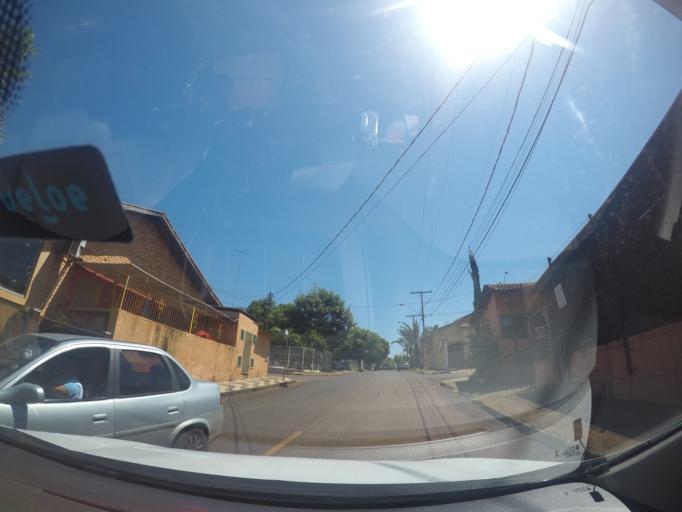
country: BR
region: Goias
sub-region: Itumbiara
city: Itumbiara
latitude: -18.4130
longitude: -49.2039
